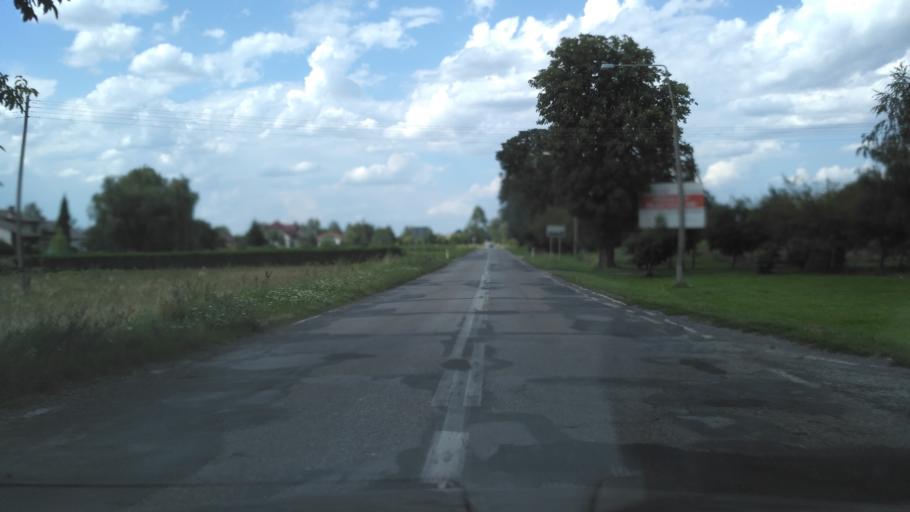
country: PL
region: Lublin Voivodeship
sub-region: Powiat leczynski
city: Milejow
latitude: 51.1979
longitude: 22.9376
